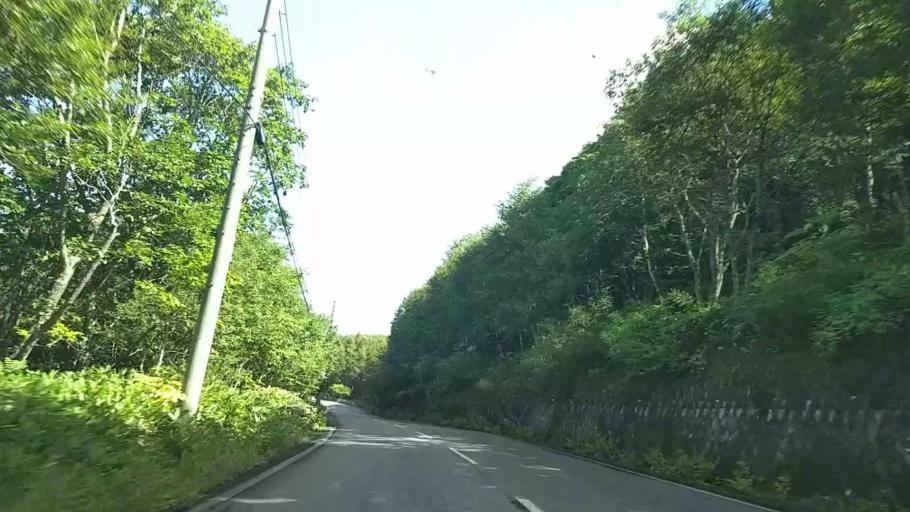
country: JP
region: Nagano
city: Suwa
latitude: 36.1101
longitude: 138.1702
